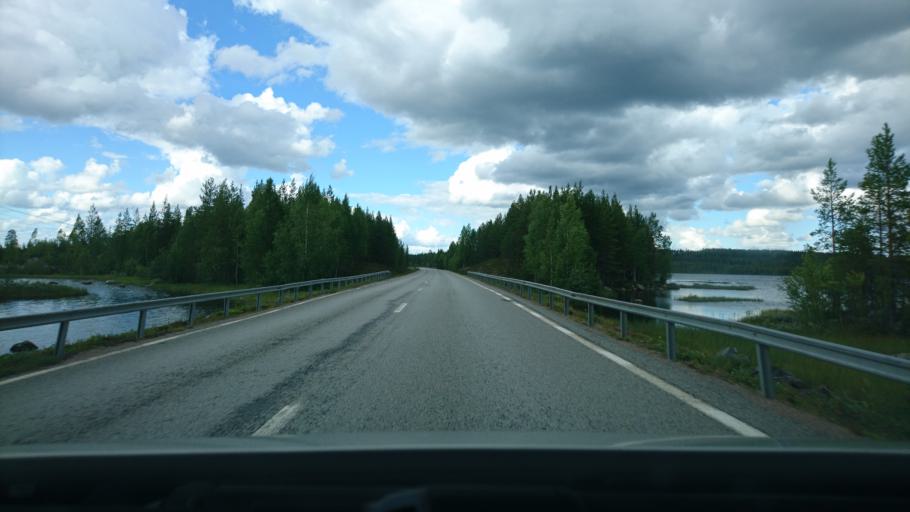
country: SE
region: Vaesterbotten
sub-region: Asele Kommun
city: Asele
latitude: 63.8944
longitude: 17.2181
